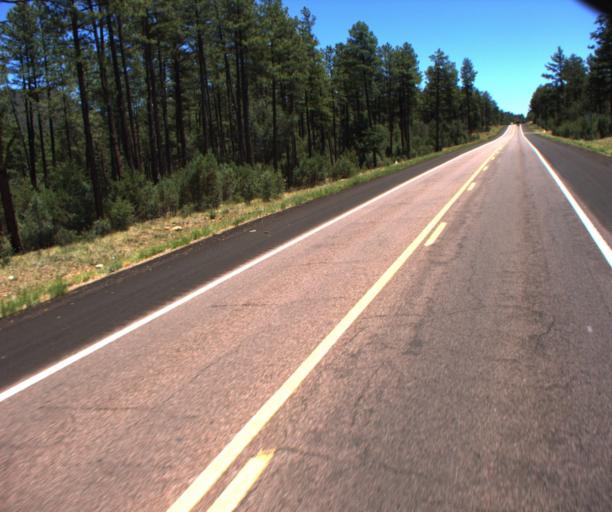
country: US
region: Arizona
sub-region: Gila County
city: Pine
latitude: 34.3702
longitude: -111.4418
